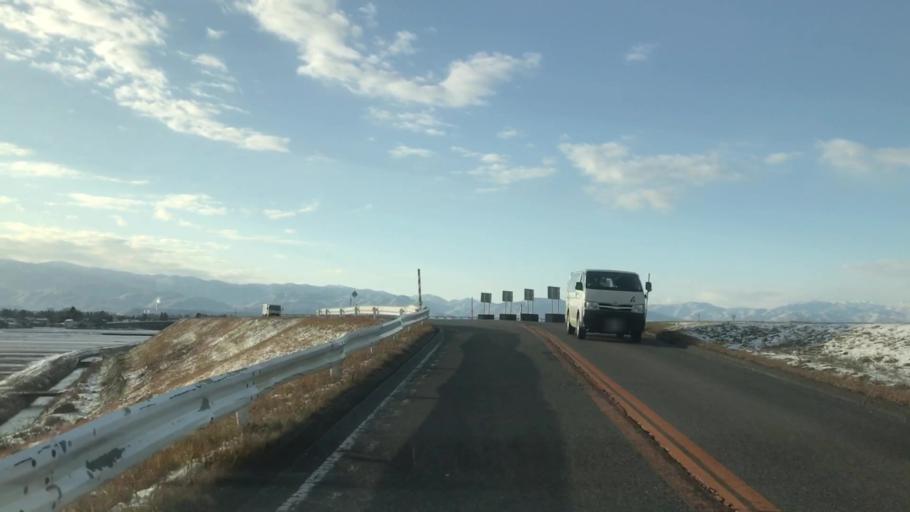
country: JP
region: Toyama
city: Toyama-shi
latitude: 36.6797
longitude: 137.2845
